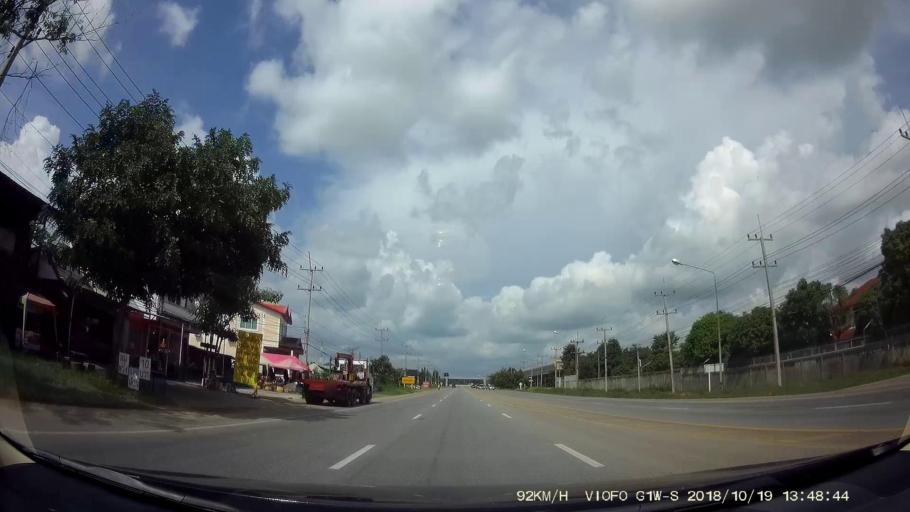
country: TH
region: Chaiyaphum
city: Chaiyaphum
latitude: 15.7297
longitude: 102.0218
